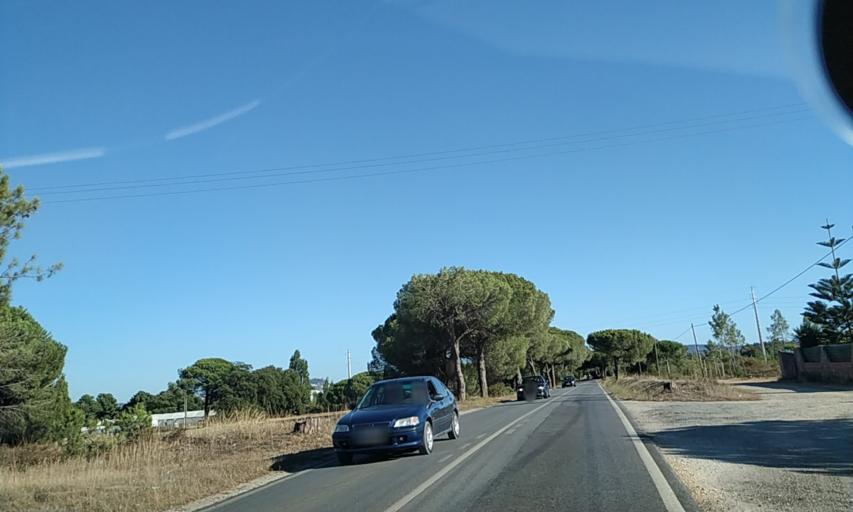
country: PT
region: Setubal
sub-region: Moita
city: Moita
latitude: 38.6237
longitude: -8.9593
